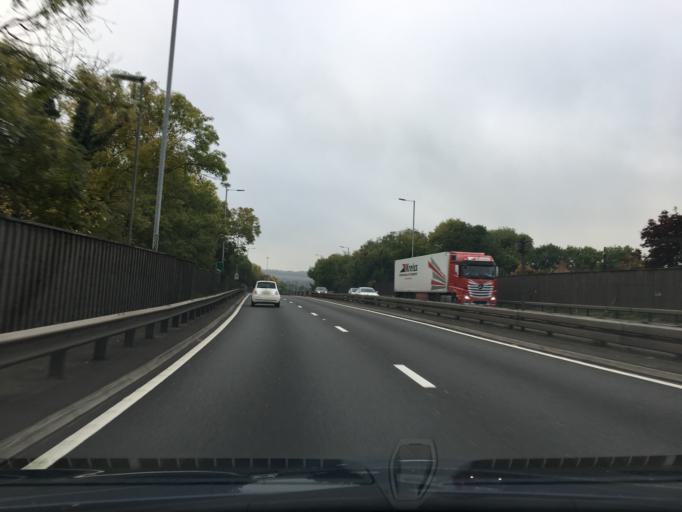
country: GB
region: England
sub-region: Surrey
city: Guildford
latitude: 51.2451
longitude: -0.5959
